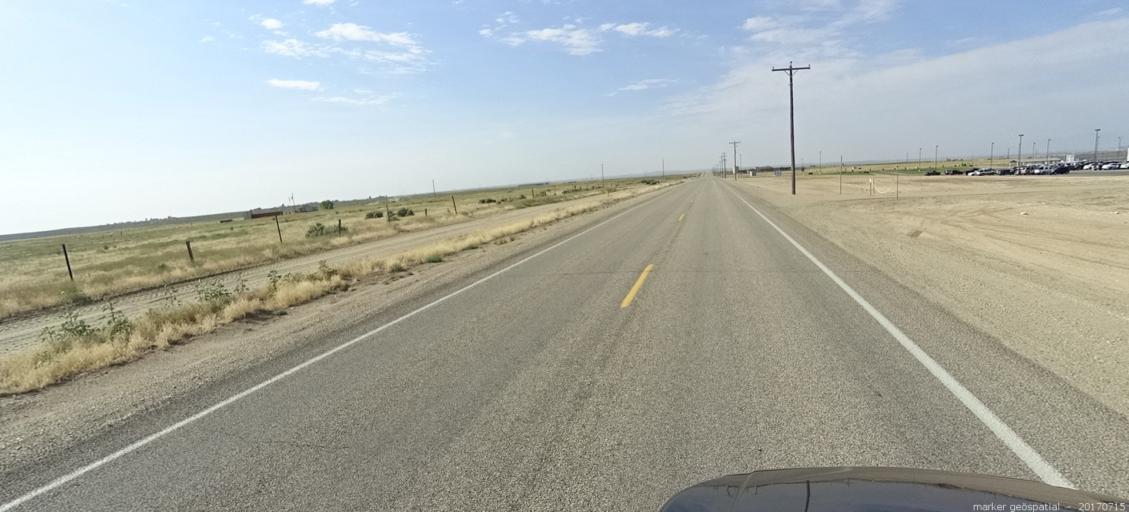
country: US
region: Idaho
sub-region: Ada County
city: Boise
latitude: 43.4716
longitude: -116.2343
